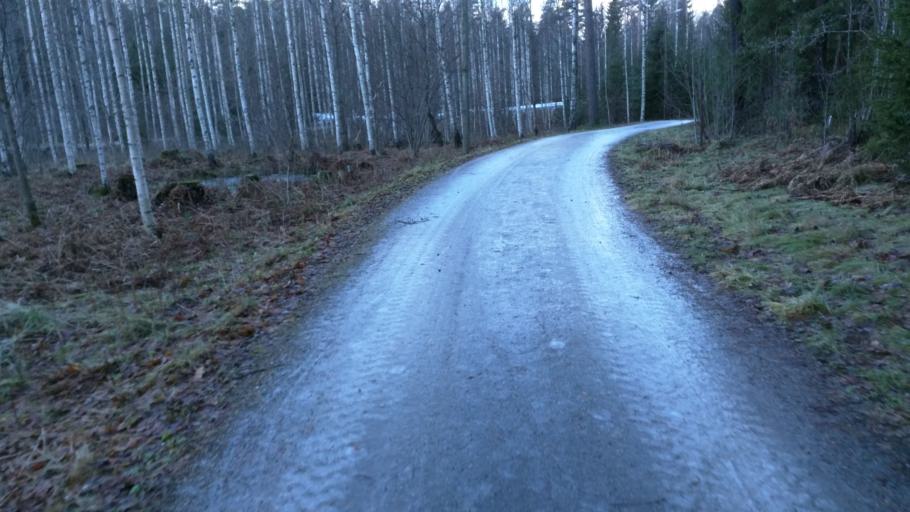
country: FI
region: Uusimaa
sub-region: Helsinki
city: Espoo
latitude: 60.2400
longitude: 24.6743
